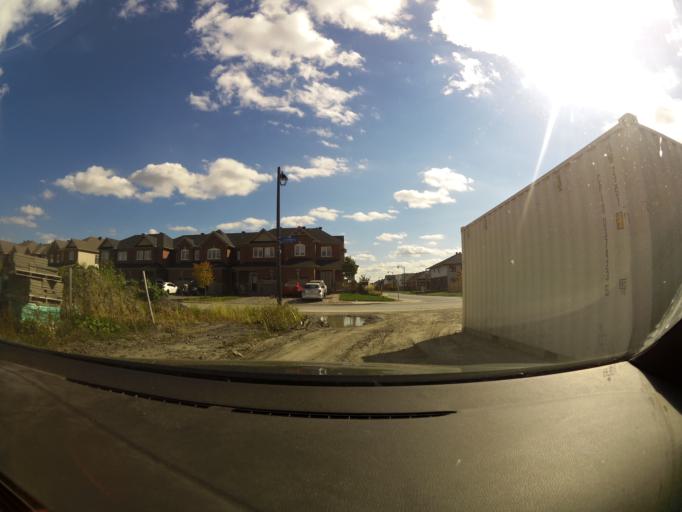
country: CA
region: Ontario
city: Bells Corners
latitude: 45.2757
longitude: -75.8902
